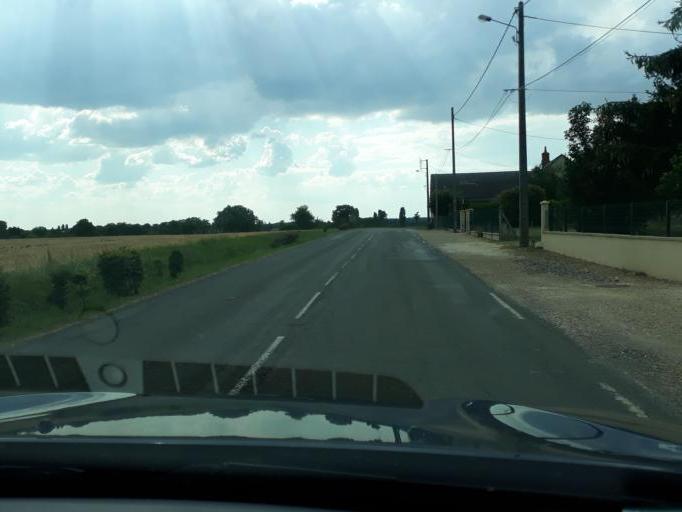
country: FR
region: Centre
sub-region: Departement du Cher
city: Baugy
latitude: 47.0937
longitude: 2.6811
